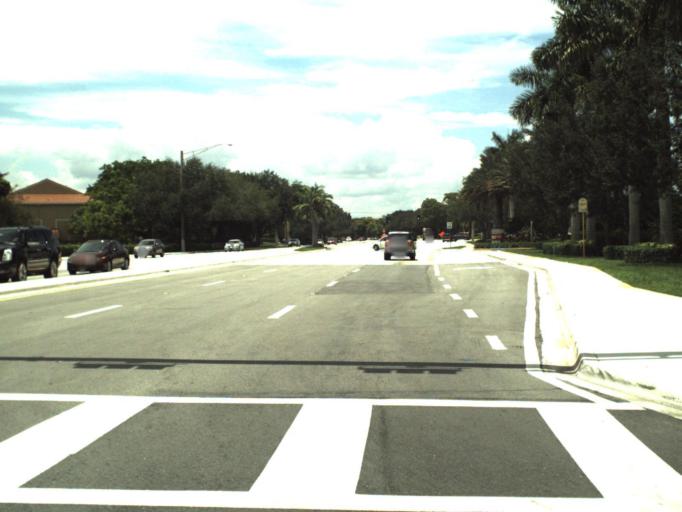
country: US
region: Florida
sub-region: Broward County
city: Tamarac
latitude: 26.2375
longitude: -80.2452
